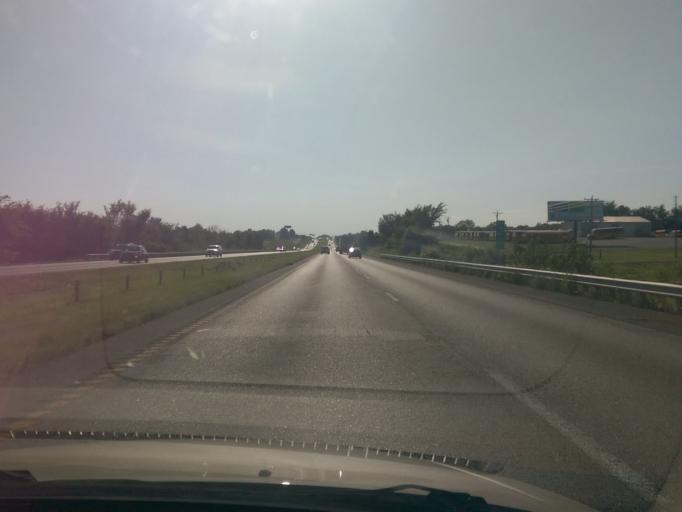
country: US
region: Missouri
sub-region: Lafayette County
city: Odessa
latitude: 39.0067
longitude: -93.9129
